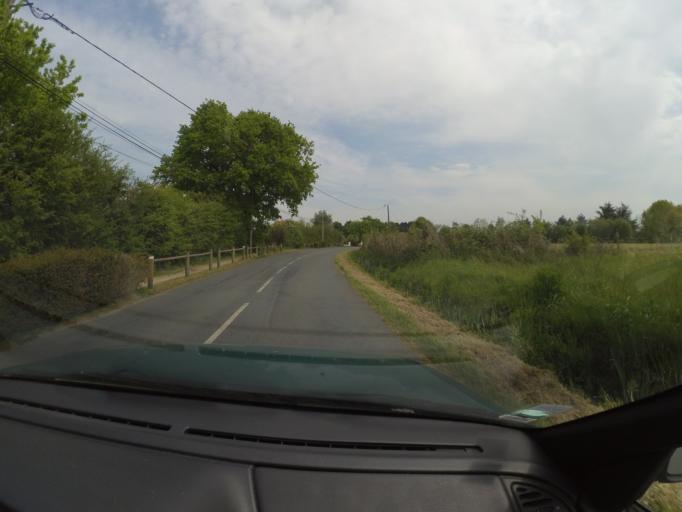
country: FR
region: Pays de la Loire
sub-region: Departement de la Loire-Atlantique
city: Saint-Hilaire-de-Clisson
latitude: 47.0624
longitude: -1.3178
